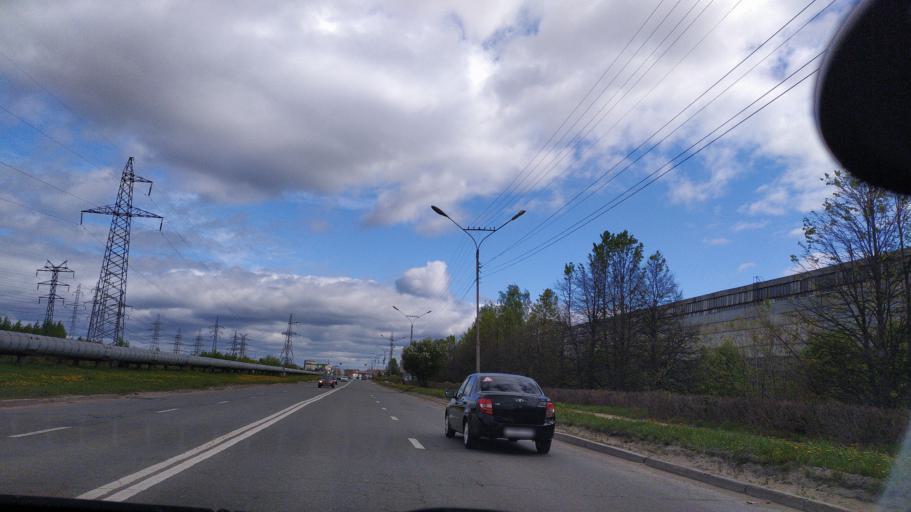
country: RU
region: Chuvashia
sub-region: Cheboksarskiy Rayon
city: Cheboksary
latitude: 56.1234
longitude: 47.3057
